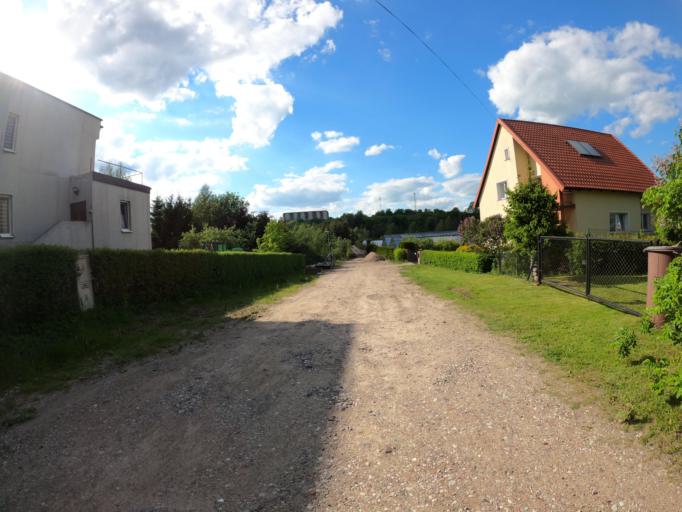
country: PL
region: Warmian-Masurian Voivodeship
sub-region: Powiat lidzbarski
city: Lidzbark Warminski
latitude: 54.1324
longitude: 20.5989
